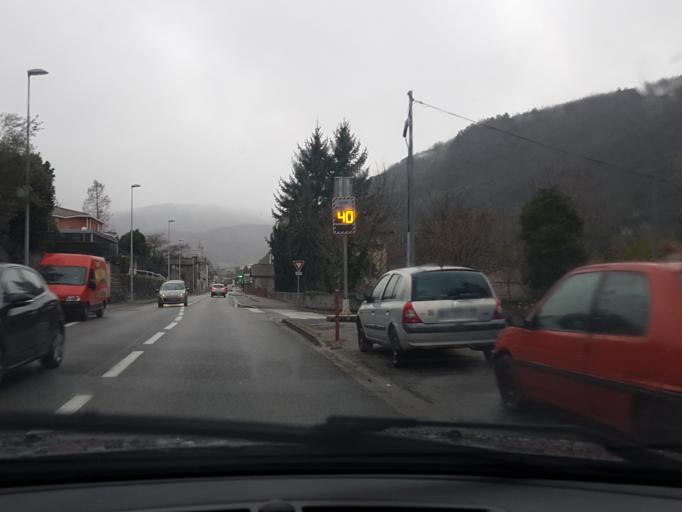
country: FR
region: Midi-Pyrenees
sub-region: Departement de l'Ariege
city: Foix
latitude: 42.9786
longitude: 1.6097
